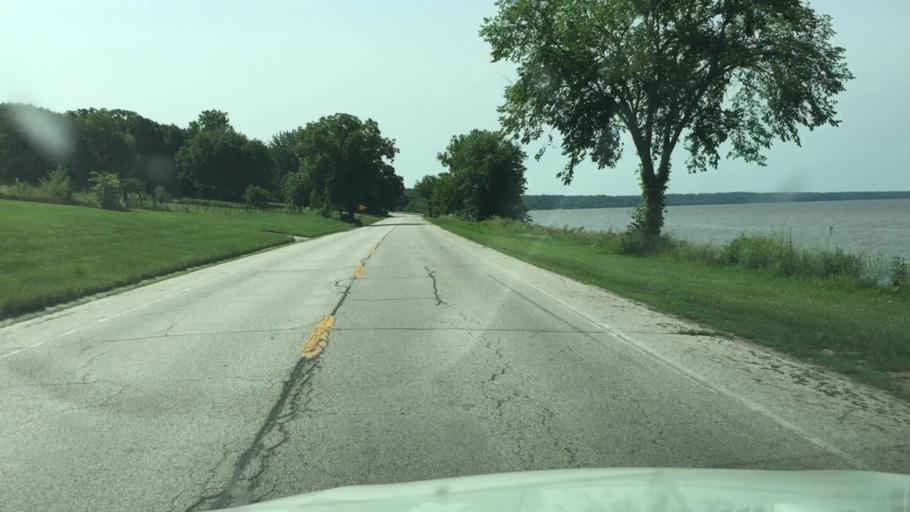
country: US
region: Illinois
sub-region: Hancock County
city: Nauvoo
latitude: 40.5242
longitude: -91.3671
